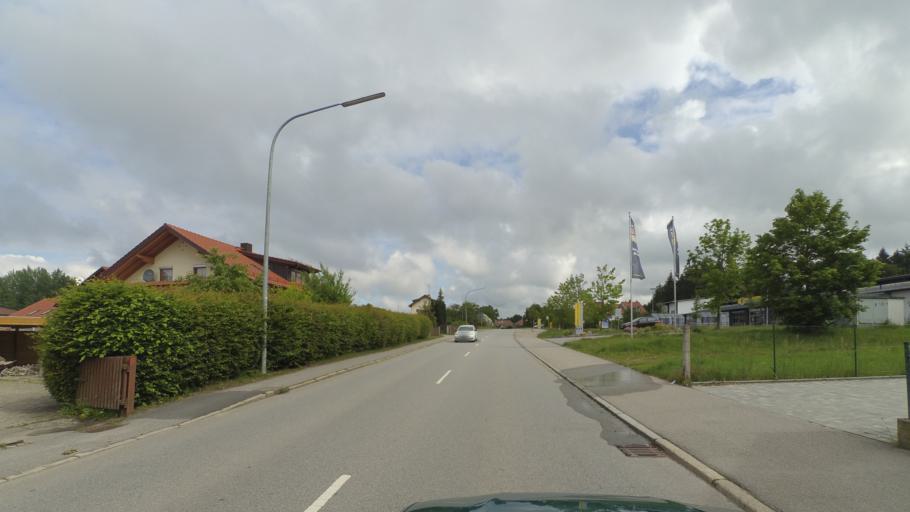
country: DE
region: Bavaria
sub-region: Lower Bavaria
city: Mitterfels
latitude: 48.9792
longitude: 12.6819
